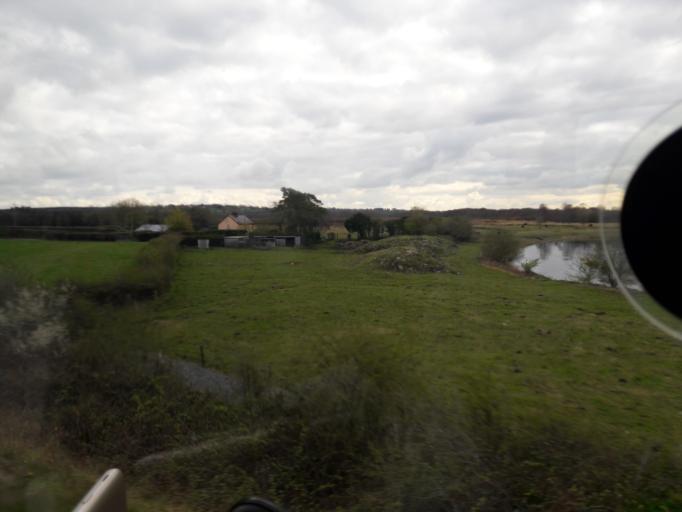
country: IE
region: Leinster
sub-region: An Longfort
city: Granard
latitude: 53.6522
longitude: -7.4333
